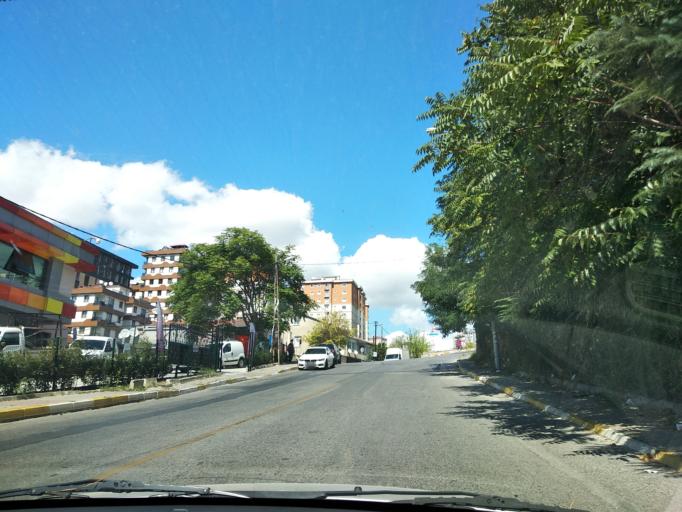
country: TR
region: Istanbul
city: Umraniye
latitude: 41.0072
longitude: 29.1074
